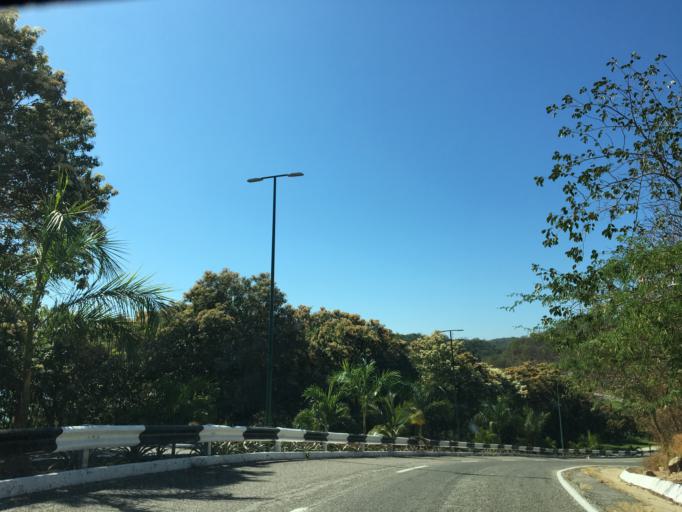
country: MX
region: Oaxaca
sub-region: Santa Maria Huatulco
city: Crucecita
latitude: 15.7814
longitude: -96.0685
